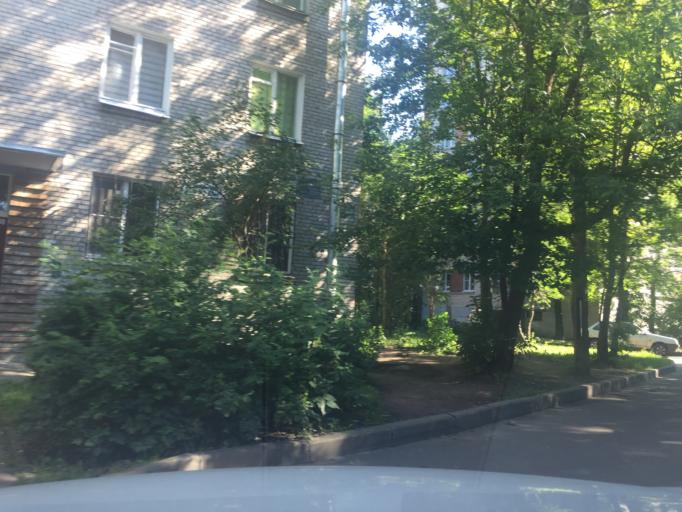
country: RU
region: St.-Petersburg
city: Pushkin
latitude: 59.7345
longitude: 30.4152
